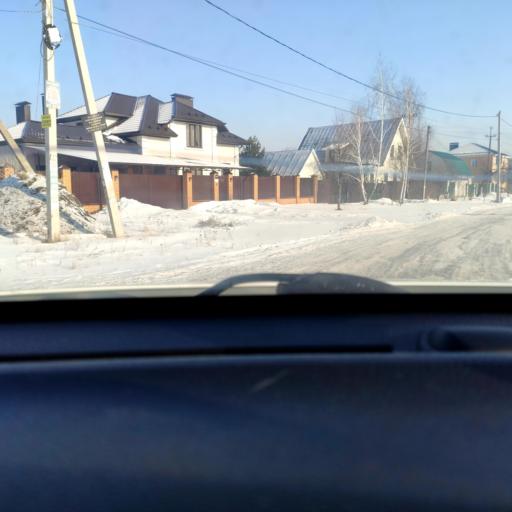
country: RU
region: Voronezj
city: Somovo
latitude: 51.6828
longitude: 39.3172
